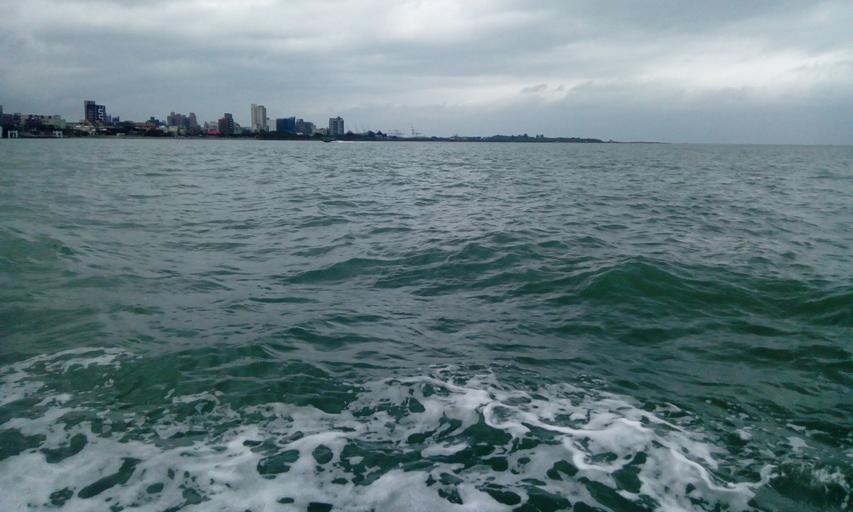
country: TW
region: Taipei
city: Taipei
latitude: 25.1637
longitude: 121.4366
